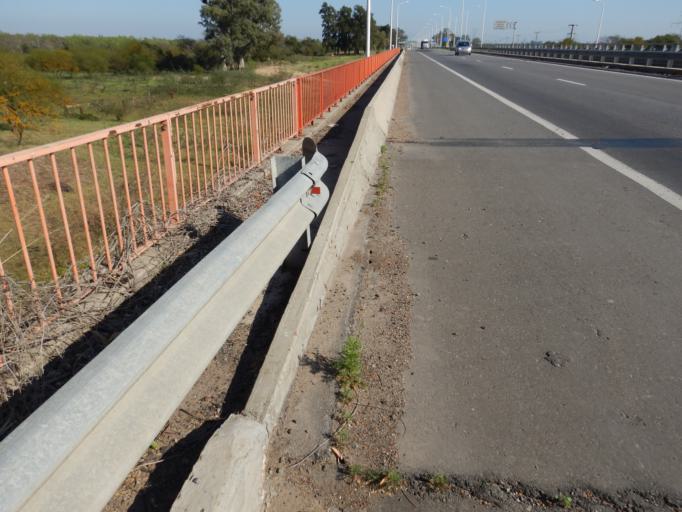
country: AR
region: Entre Rios
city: Parana
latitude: -31.6695
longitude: -60.5818
